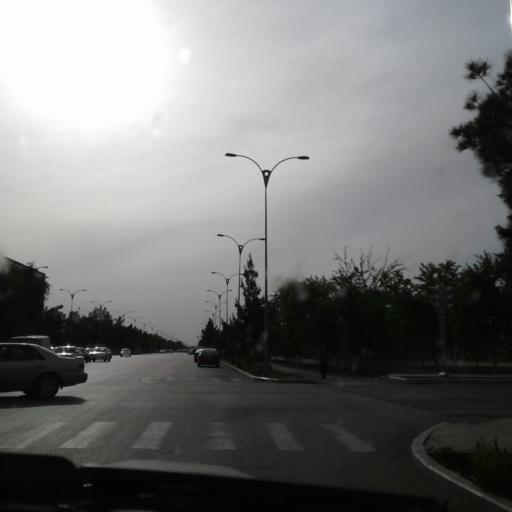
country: TM
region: Mary
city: Mary
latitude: 37.5897
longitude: 61.8362
